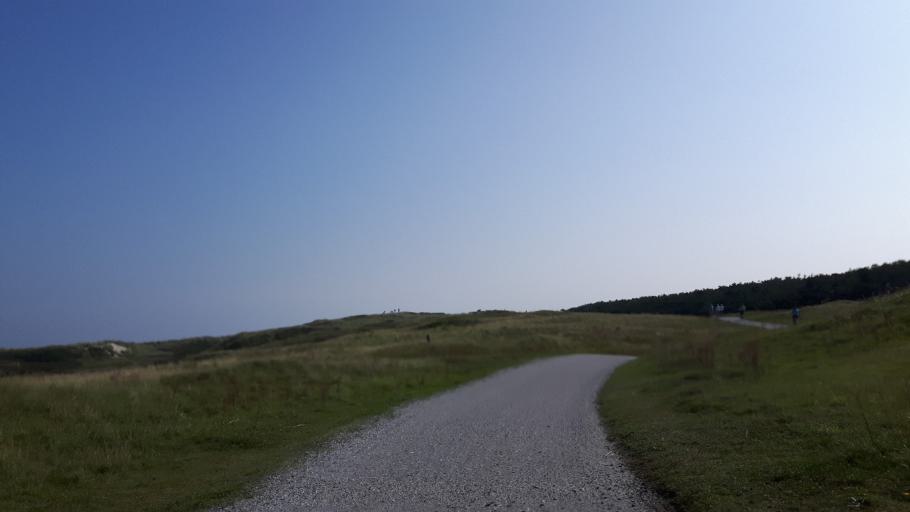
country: NL
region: Friesland
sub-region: Gemeente Ameland
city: Nes
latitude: 53.4593
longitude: 5.8005
